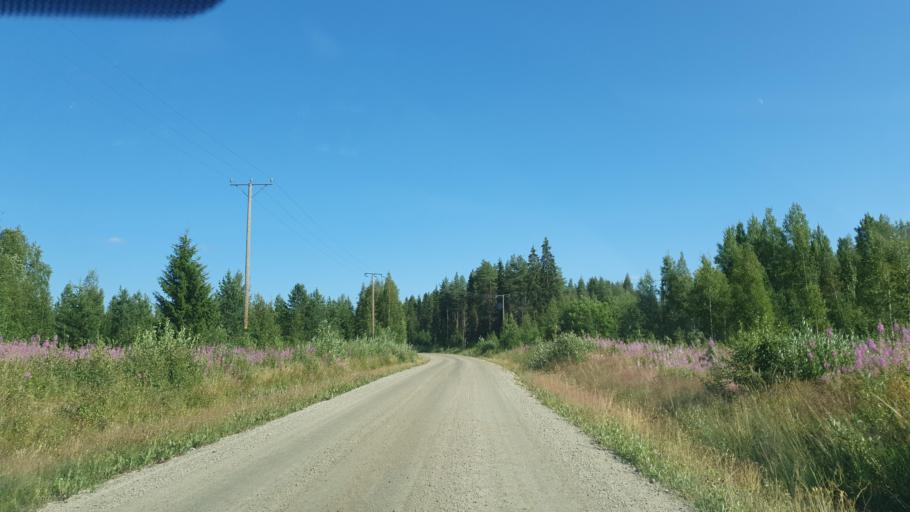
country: FI
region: Kainuu
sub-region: Kehys-Kainuu
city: Kuhmo
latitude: 64.0478
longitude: 29.6228
